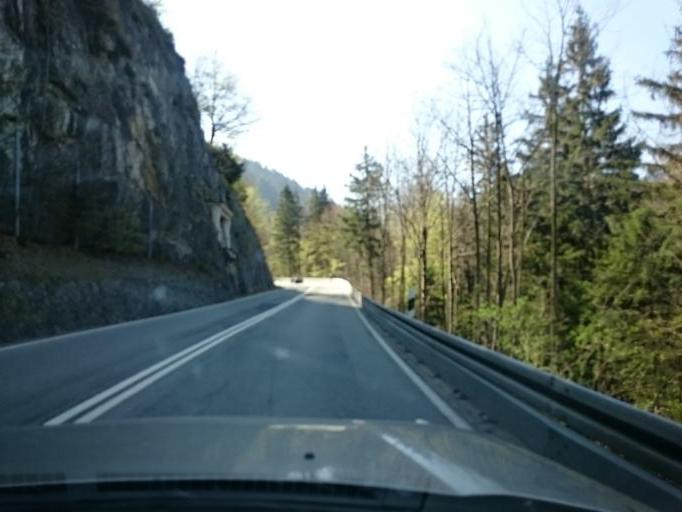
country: DE
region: Bavaria
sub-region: Upper Bavaria
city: Kochel
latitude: 47.6314
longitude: 11.3540
